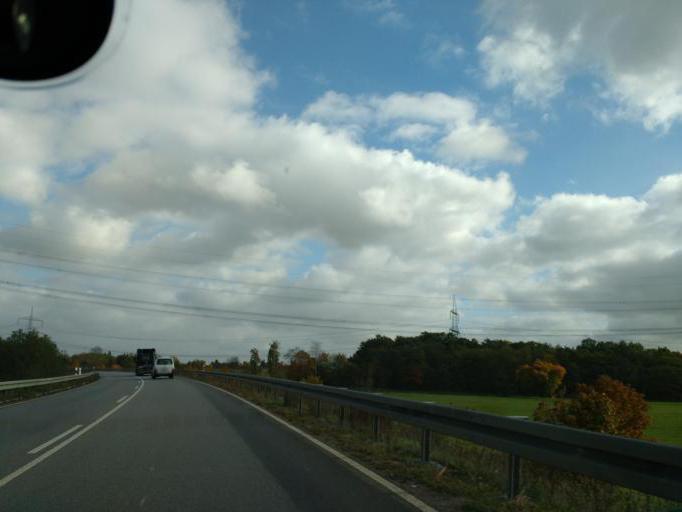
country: DE
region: Brandenburg
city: Altlandsberg
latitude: 52.5443
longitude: 13.7205
